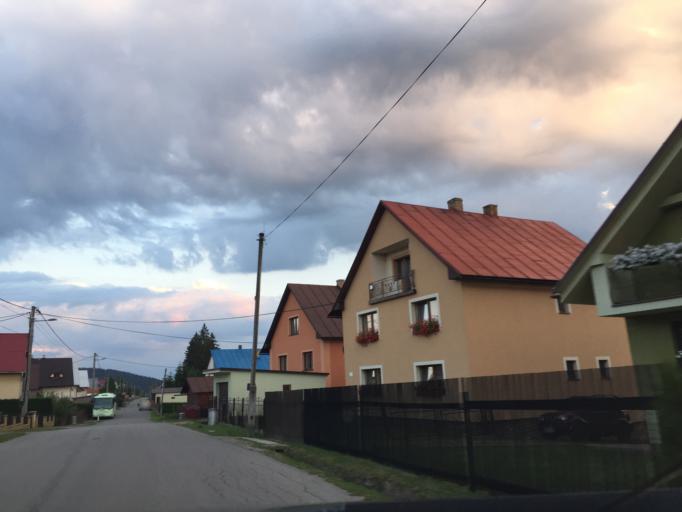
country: PL
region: Silesian Voivodeship
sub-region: Powiat zywiecki
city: Sopotnia Wielka
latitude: 49.4662
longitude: 19.2976
